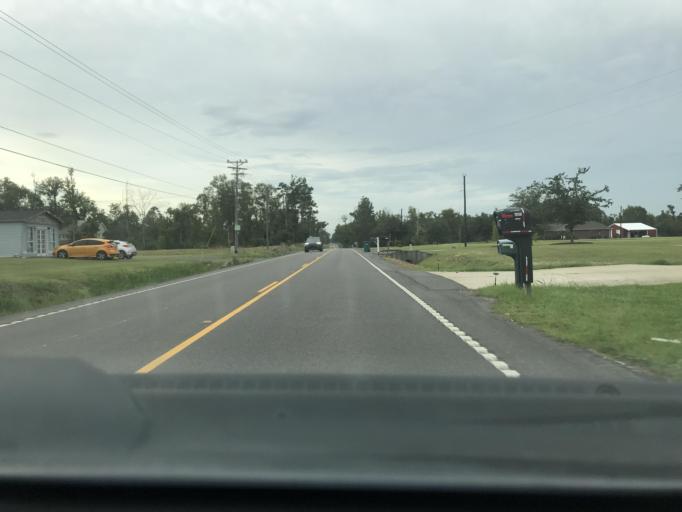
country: US
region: Louisiana
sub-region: Calcasieu Parish
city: Moss Bluff
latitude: 30.3320
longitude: -93.2580
